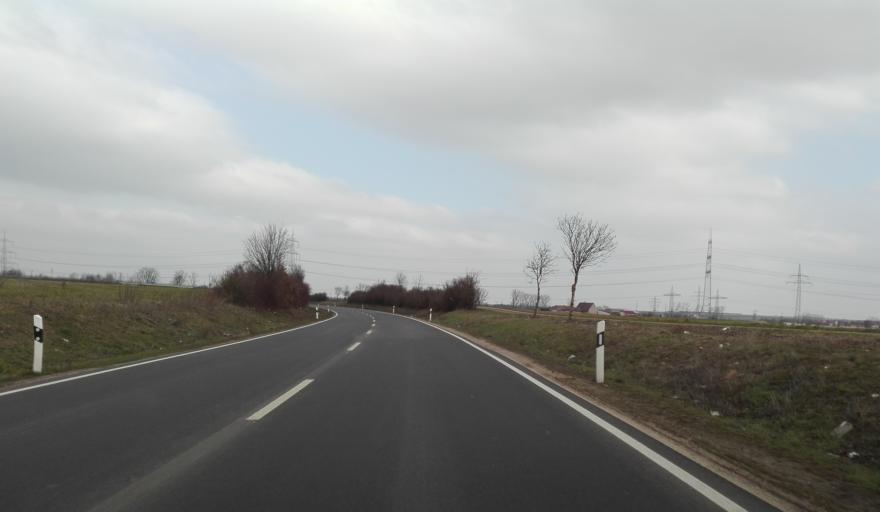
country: DE
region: Rheinland-Pfalz
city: Kirchheim an der Weinstrasse
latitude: 49.5596
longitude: 8.1889
